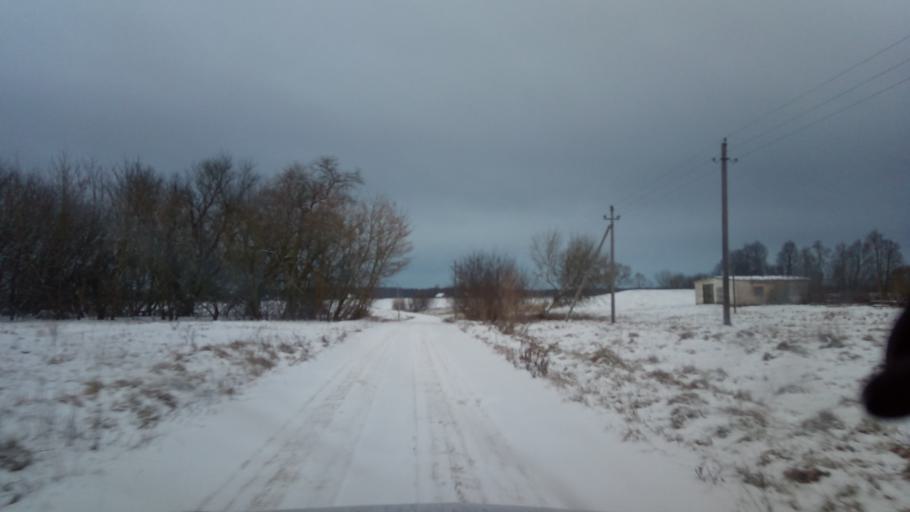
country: LT
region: Vilnius County
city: Ukmerge
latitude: 55.4794
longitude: 24.6194
